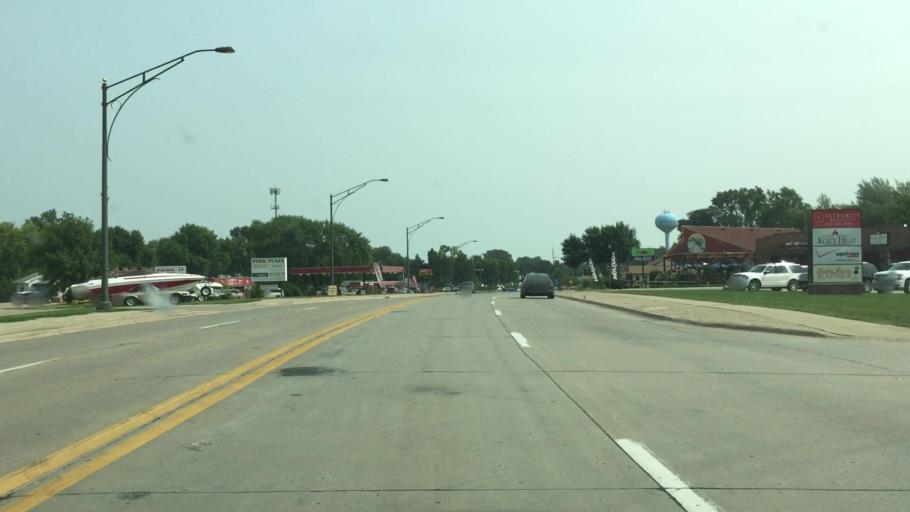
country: US
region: Iowa
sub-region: Dickinson County
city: Arnolds Park
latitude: 43.3618
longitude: -95.1401
